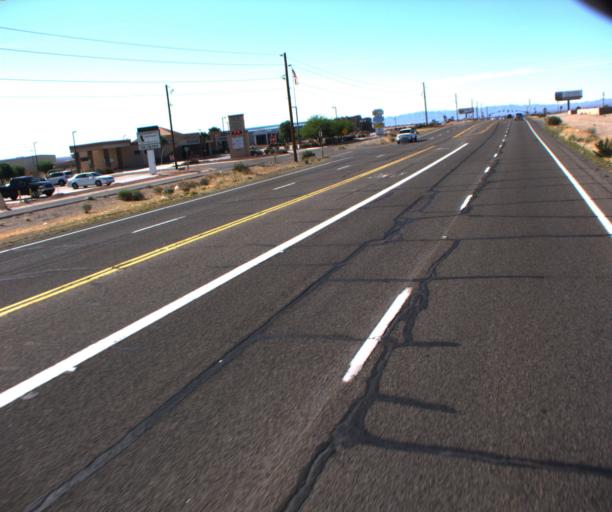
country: US
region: Arizona
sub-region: Mohave County
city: Mohave Valley
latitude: 34.9874
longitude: -114.5981
